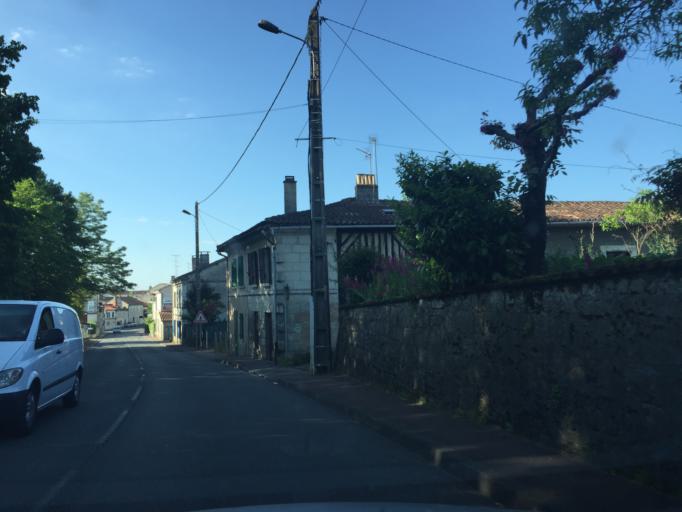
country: FR
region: Aquitaine
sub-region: Departement de la Dordogne
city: La Roche-Chalais
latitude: 45.1495
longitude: 0.0081
